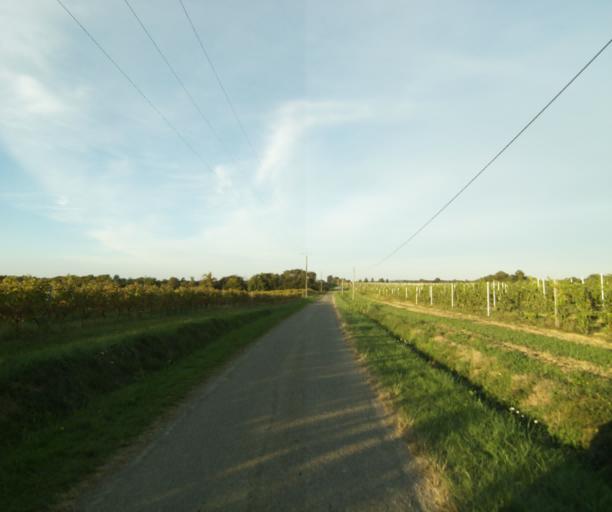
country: FR
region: Midi-Pyrenees
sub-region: Departement du Gers
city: Eauze
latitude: 43.8807
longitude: 0.0431
